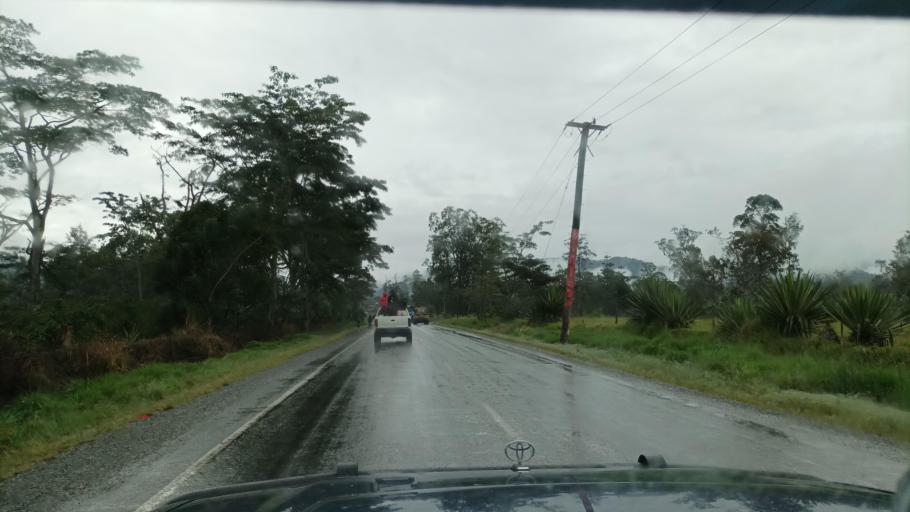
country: PG
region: Western Highlands
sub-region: Hagen
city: Mount Hagen
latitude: -5.8391
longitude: 144.3213
